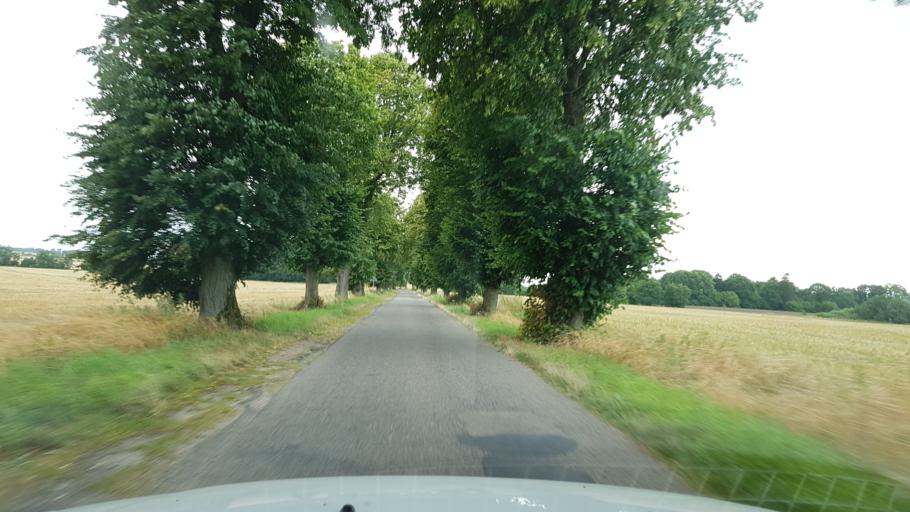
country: PL
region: West Pomeranian Voivodeship
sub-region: Powiat bialogardzki
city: Karlino
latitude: 54.1156
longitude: 15.8713
